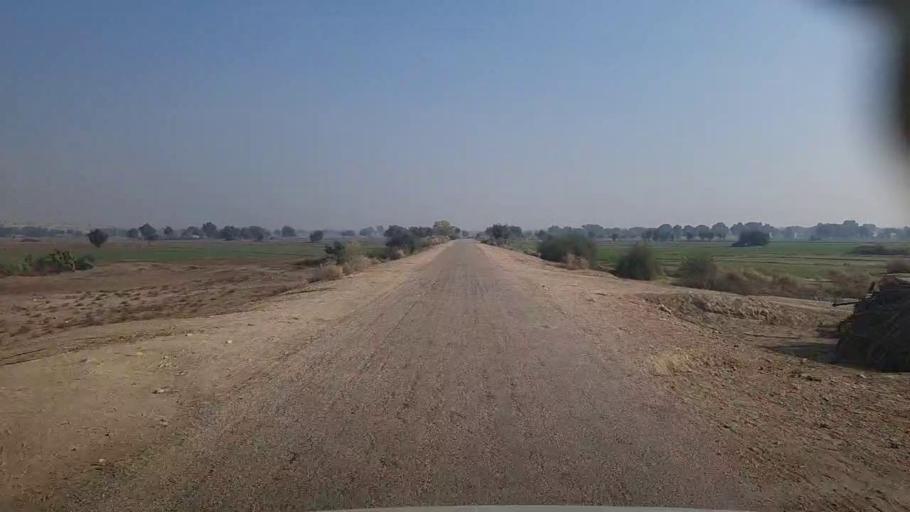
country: PK
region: Sindh
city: Kandiari
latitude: 26.8210
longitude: 68.4920
